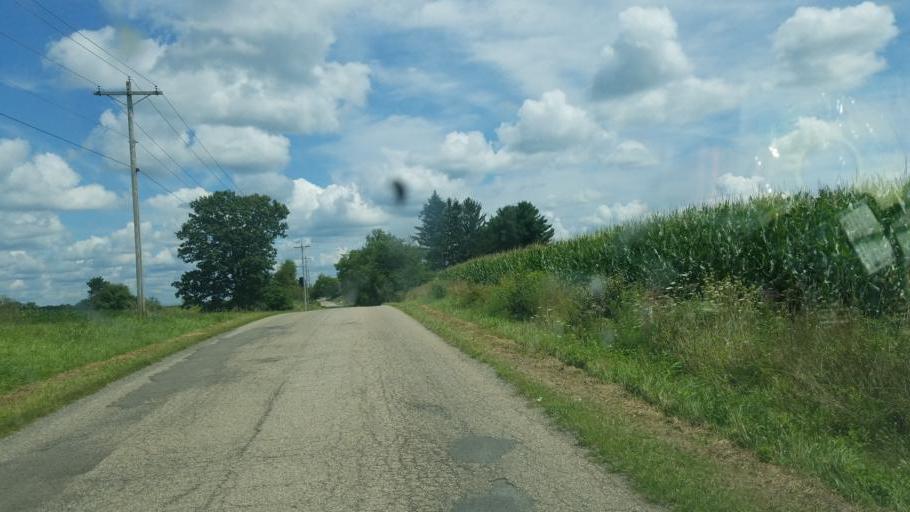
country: US
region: Ohio
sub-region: Knox County
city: Centerburg
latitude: 40.3731
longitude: -82.6866
